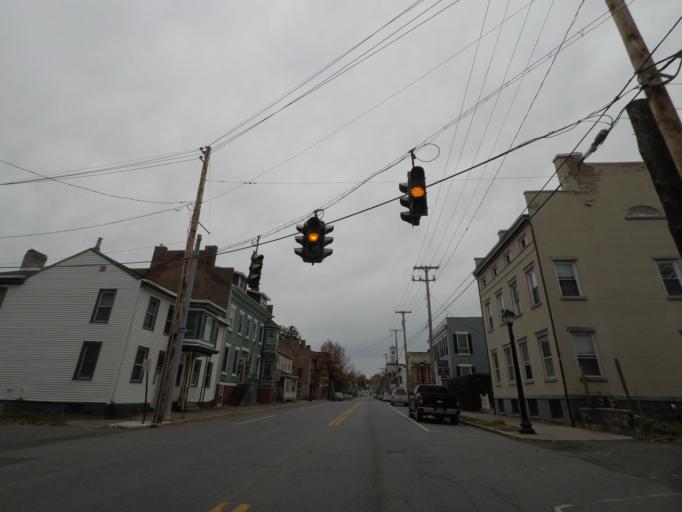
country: US
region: New York
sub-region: Saratoga County
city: Waterford
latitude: 42.7896
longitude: -73.6765
